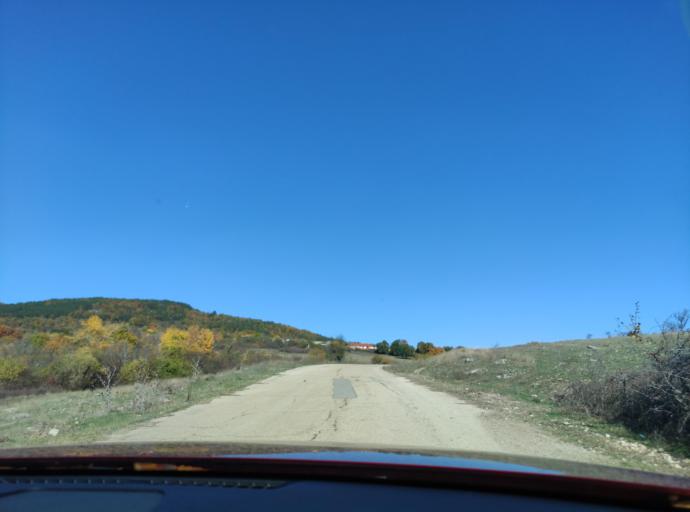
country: BG
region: Montana
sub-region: Obshtina Chiprovtsi
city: Chiprovtsi
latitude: 43.4504
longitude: 23.0462
